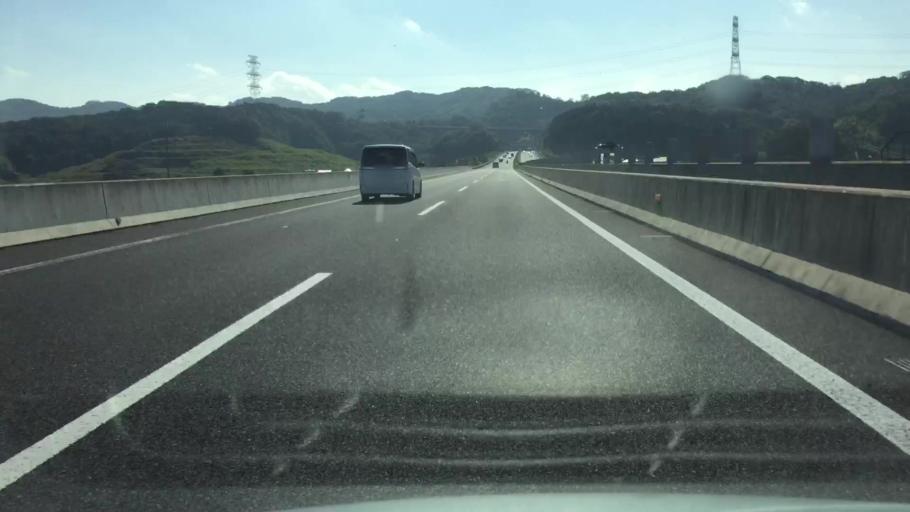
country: JP
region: Tochigi
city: Mooka
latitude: 36.3863
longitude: 140.0243
